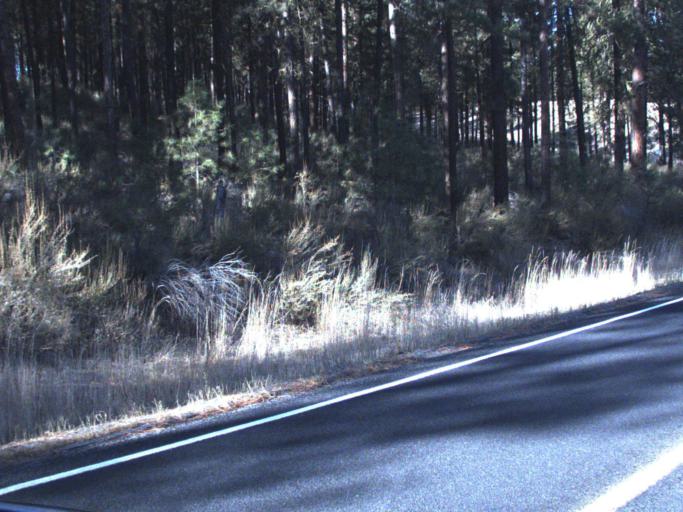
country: US
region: Washington
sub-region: Lincoln County
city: Davenport
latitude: 48.0190
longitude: -118.2367
